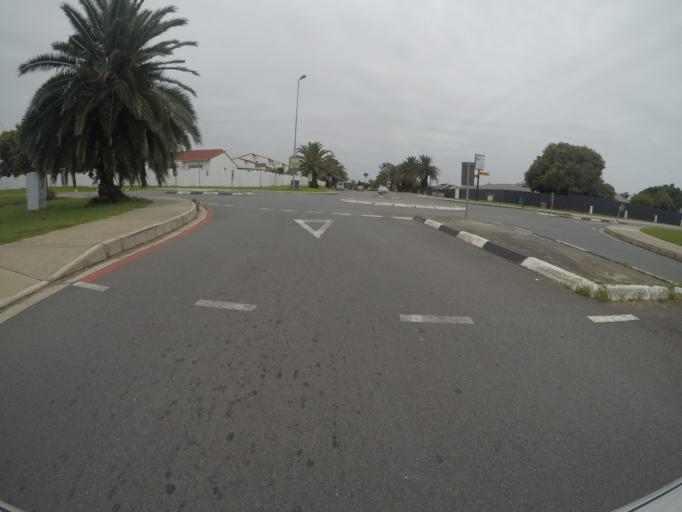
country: ZA
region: Eastern Cape
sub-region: Buffalo City Metropolitan Municipality
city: East London
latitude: -32.9763
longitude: 27.9408
